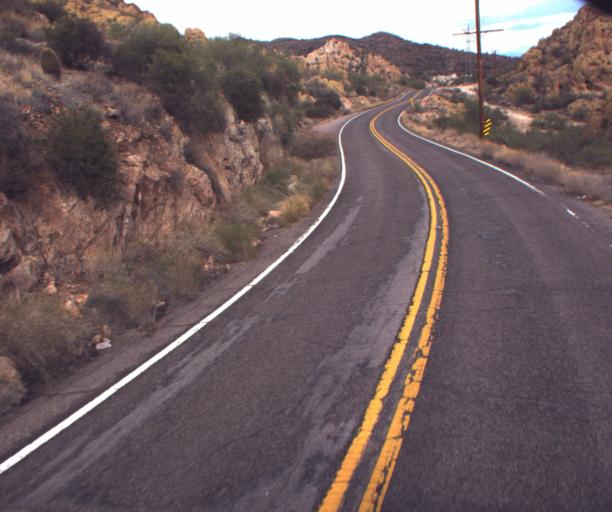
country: US
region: Arizona
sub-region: Pinal County
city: Apache Junction
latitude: 33.5315
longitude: -111.4542
